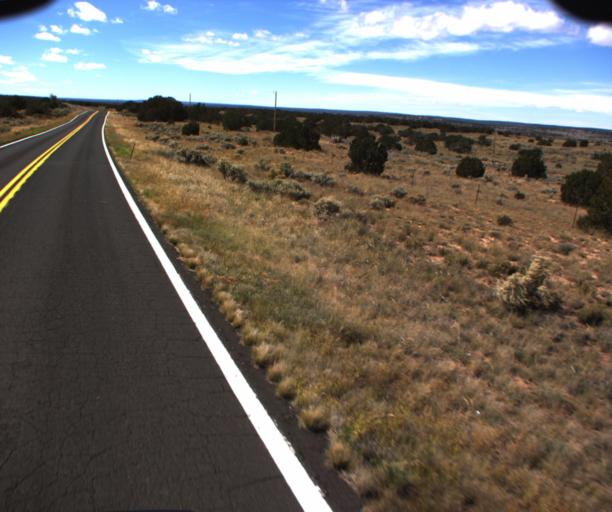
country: US
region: Arizona
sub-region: Apache County
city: Houck
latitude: 34.9218
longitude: -109.2073
